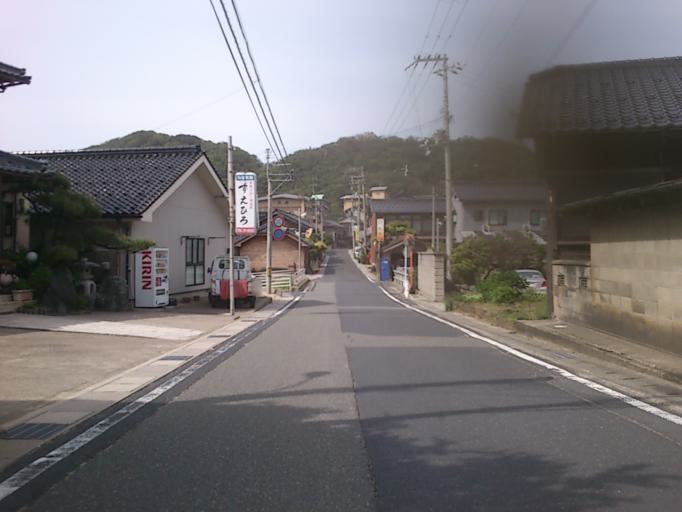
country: JP
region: Hyogo
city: Toyooka
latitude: 35.6659
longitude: 134.9679
